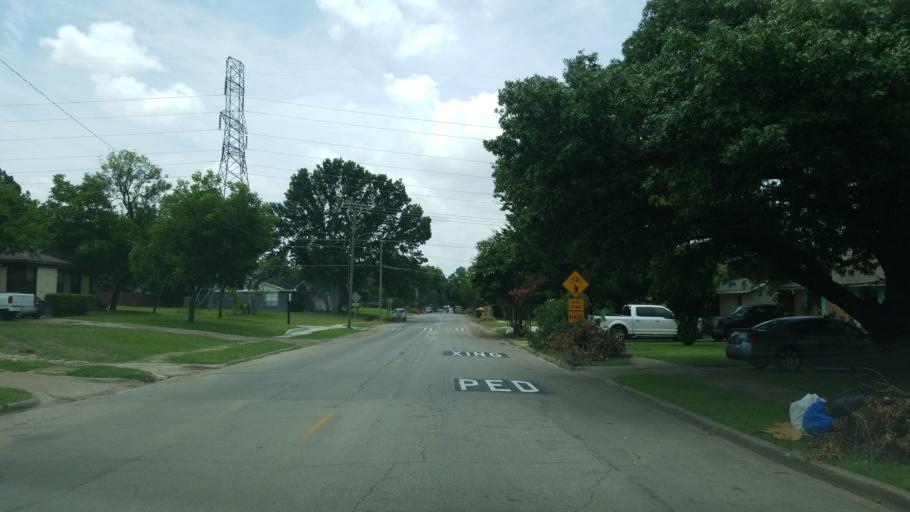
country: US
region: Texas
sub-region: Dallas County
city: Farmers Branch
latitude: 32.8856
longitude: -96.8771
